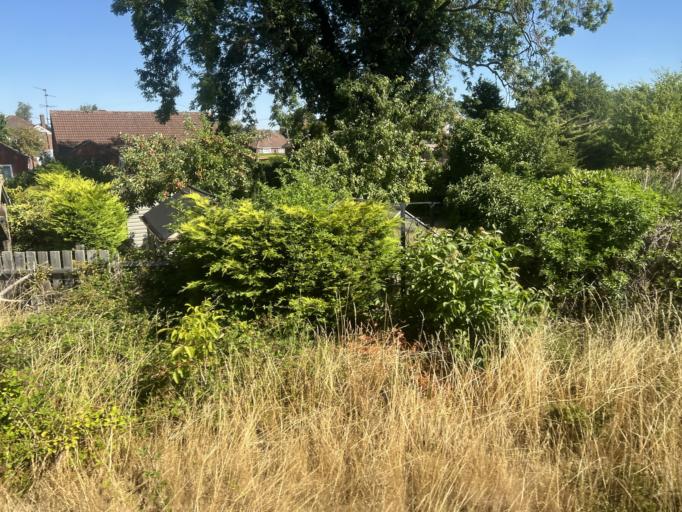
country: GB
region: England
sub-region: Lincolnshire
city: Heckington
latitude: 52.9796
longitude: -0.3077
